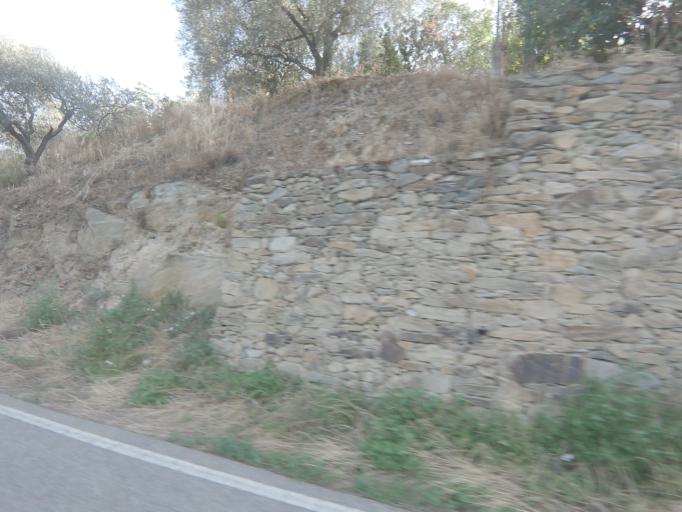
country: PT
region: Vila Real
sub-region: Sabrosa
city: Vilela
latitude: 41.2049
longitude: -7.5328
